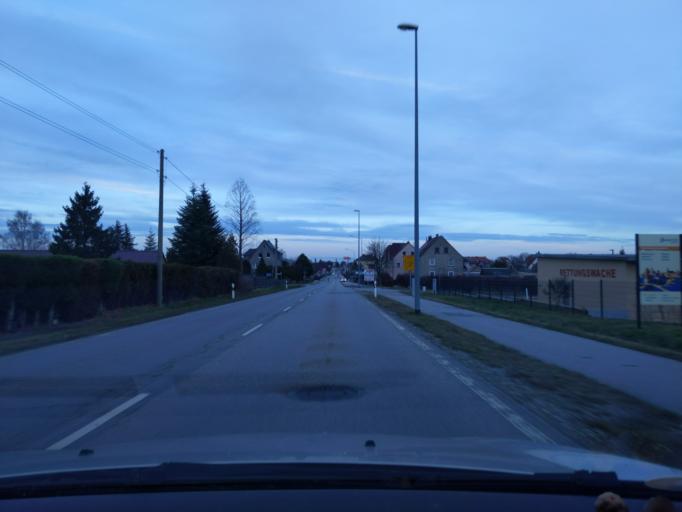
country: DE
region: Saxony
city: Bautzen
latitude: 51.1796
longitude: 14.3893
